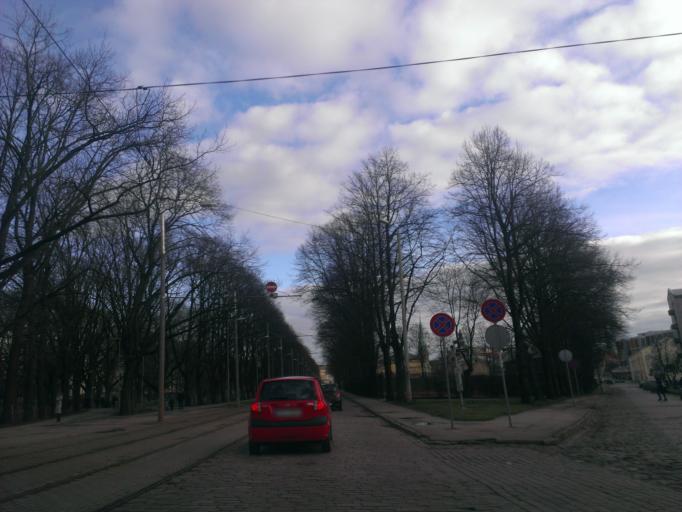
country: LV
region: Riga
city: Riga
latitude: 56.9573
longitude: 24.1008
